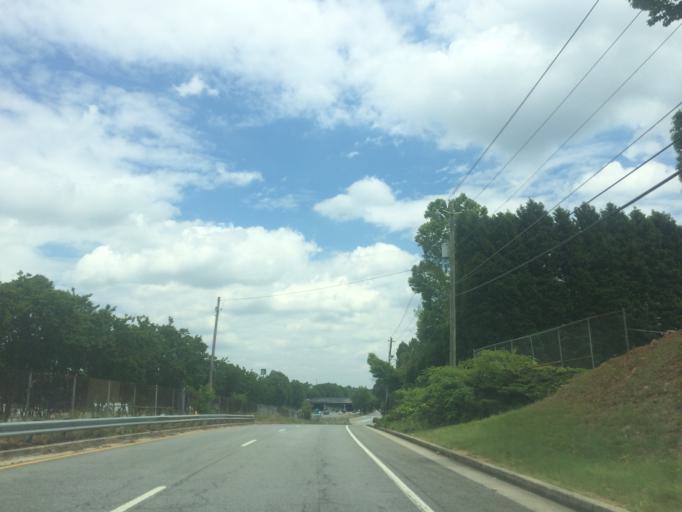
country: US
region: Georgia
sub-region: DeKalb County
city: Chamblee
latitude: 33.8610
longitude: -84.2918
